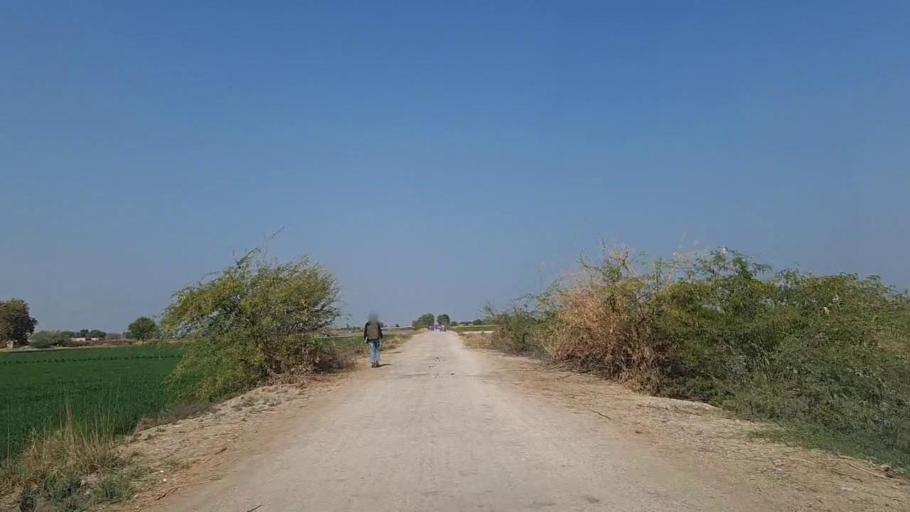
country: PK
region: Sindh
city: Nawabshah
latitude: 26.2671
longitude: 68.5133
